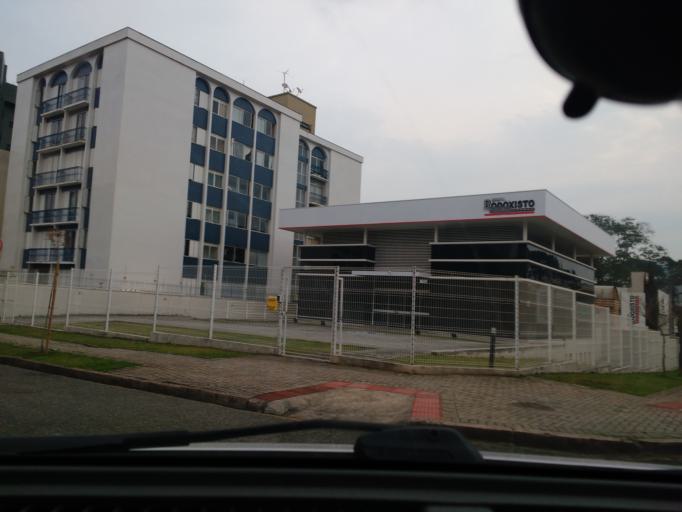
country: BR
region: Parana
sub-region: Curitiba
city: Curitiba
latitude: -25.4257
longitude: -49.2845
